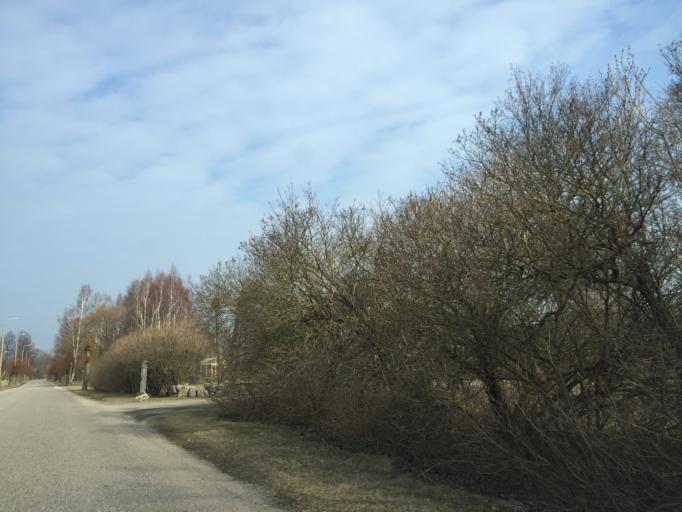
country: LV
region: Salacgrivas
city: Ainazi
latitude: 57.8673
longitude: 24.3598
